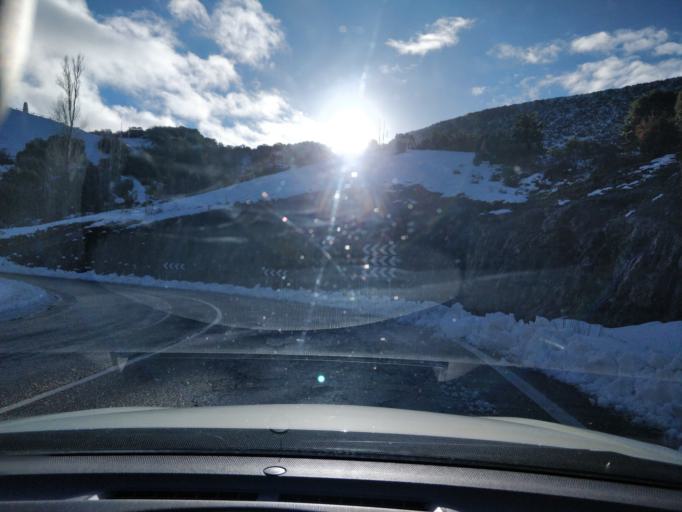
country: ES
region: Castille and Leon
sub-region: Provincia de Burgos
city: Rucandio
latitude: 42.8416
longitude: -3.6103
